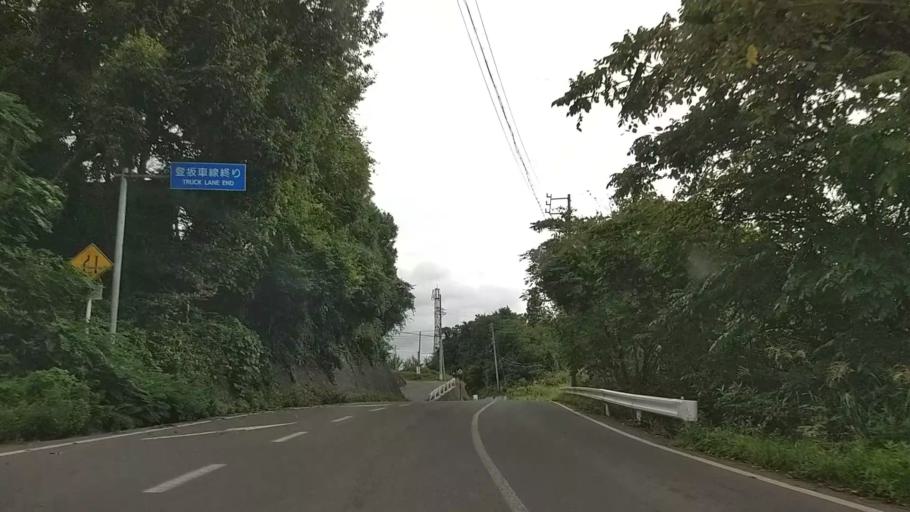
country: JP
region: Nagano
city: Nakano
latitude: 36.7813
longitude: 138.3321
